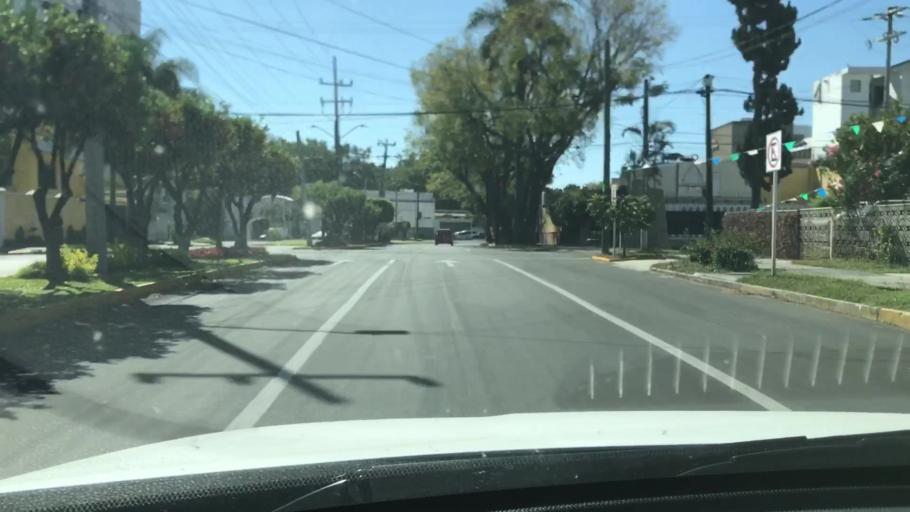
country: MX
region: Jalisco
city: Guadalajara
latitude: 20.6468
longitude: -103.4079
